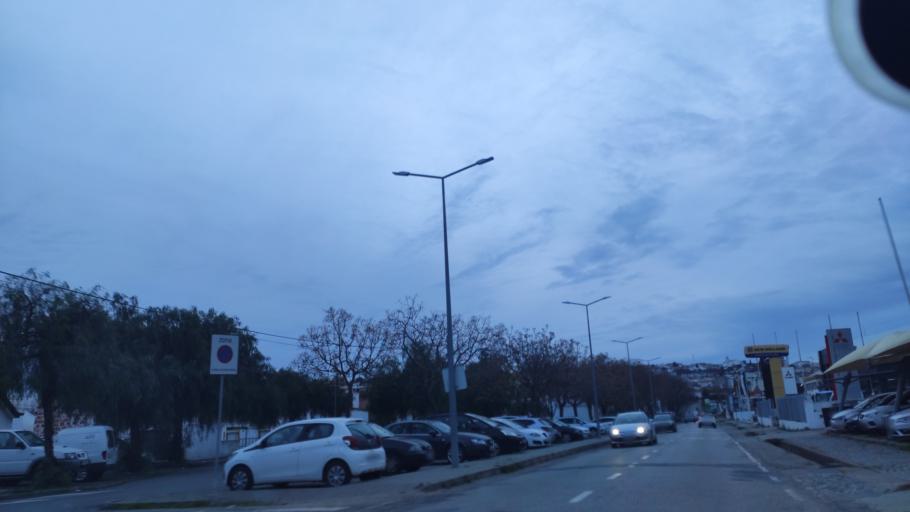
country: PT
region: Beja
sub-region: Beja
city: Beja
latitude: 38.0200
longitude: -7.8496
